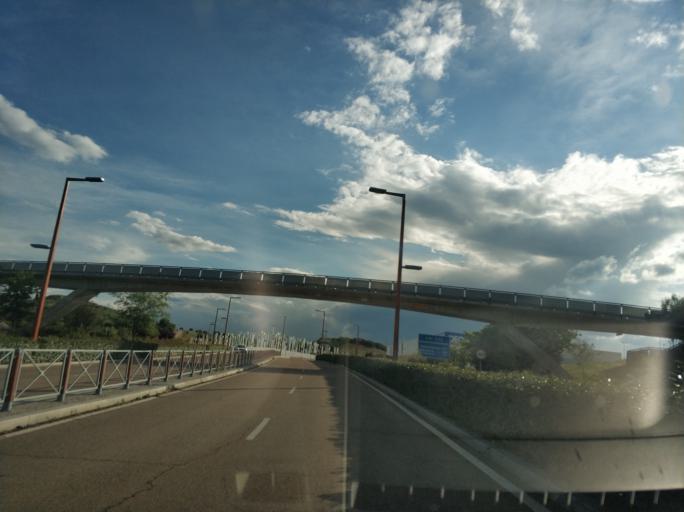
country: ES
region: Castille and Leon
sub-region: Provincia de Valladolid
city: Arroyo
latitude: 41.6186
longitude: -4.7848
